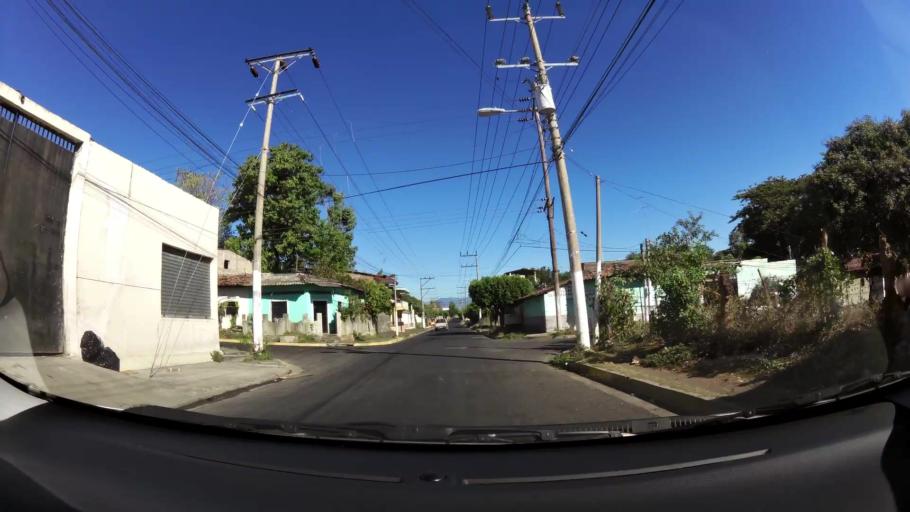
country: SV
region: San Miguel
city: San Miguel
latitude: 13.4887
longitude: -88.1769
